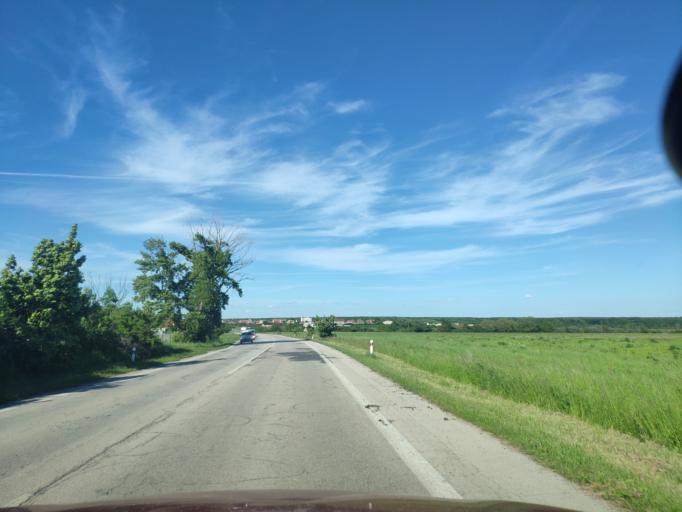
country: SK
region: Bratislavsky
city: Modra
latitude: 48.3575
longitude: 17.3294
